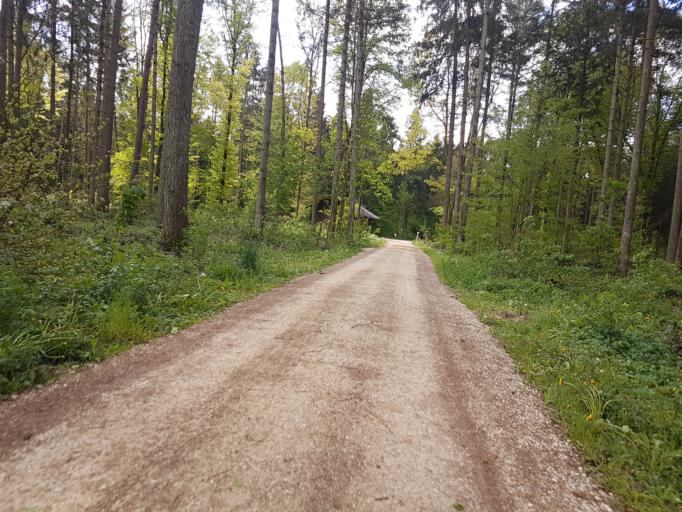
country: CH
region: Aargau
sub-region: Bezirk Zofingen
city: Fulenbach
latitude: 47.2905
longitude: 7.8390
